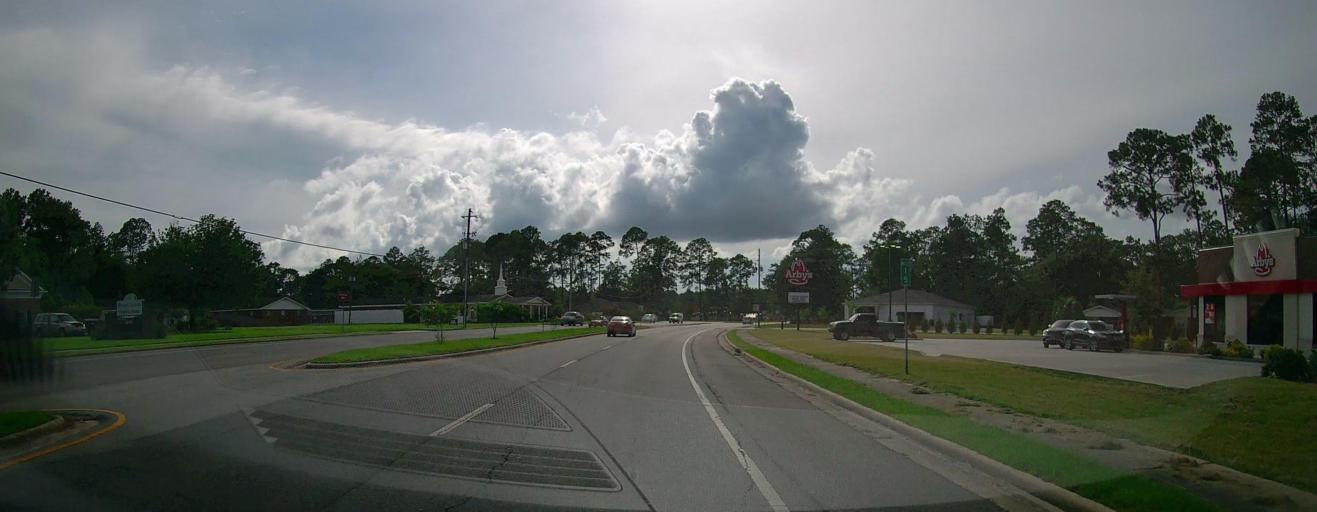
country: US
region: Georgia
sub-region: Wayne County
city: Jesup
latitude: 31.6018
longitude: -81.8942
